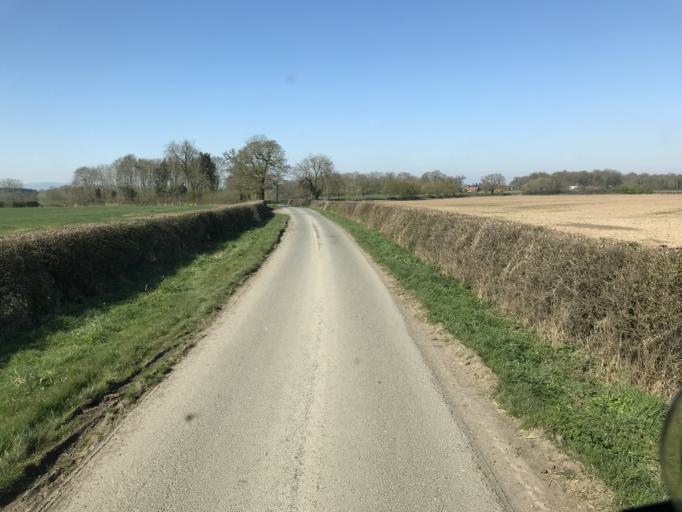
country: GB
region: England
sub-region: Cheshire West and Chester
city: Aldford
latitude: 53.1265
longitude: -2.8535
